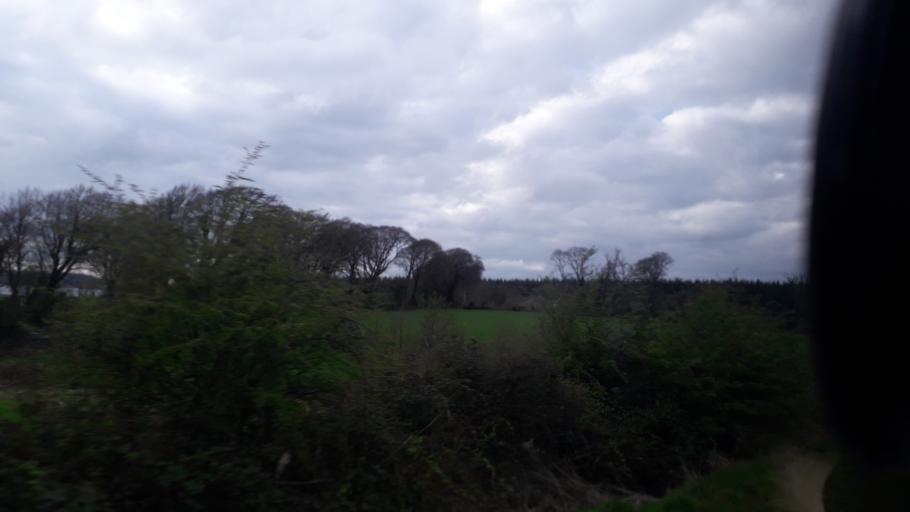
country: IE
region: Leinster
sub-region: An Iarmhi
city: An Muileann gCearr
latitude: 53.5874
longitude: -7.3835
